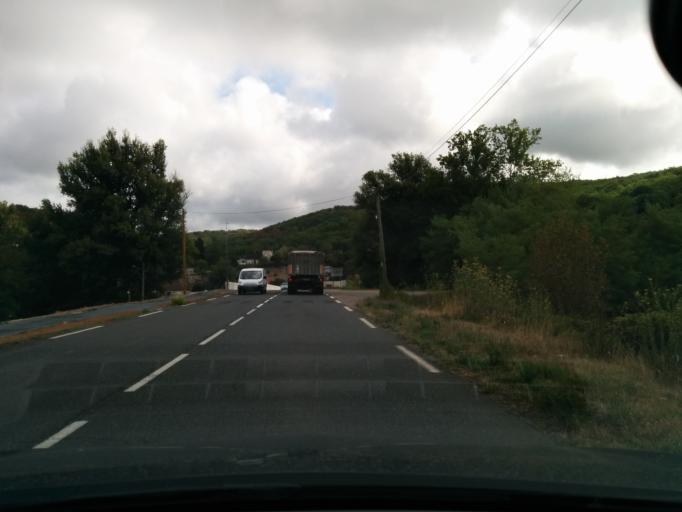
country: FR
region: Midi-Pyrenees
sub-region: Departement du Lot
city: Souillac
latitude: 44.8818
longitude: 1.4836
